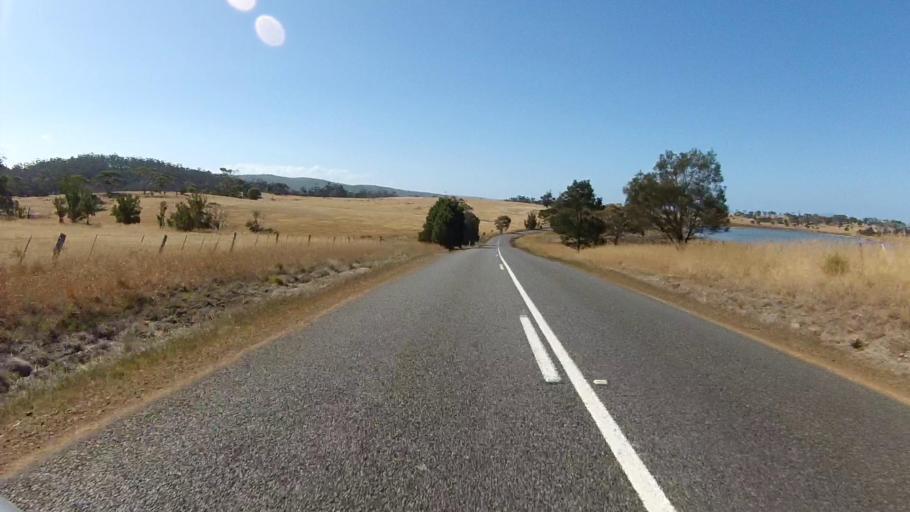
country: AU
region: Tasmania
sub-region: Sorell
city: Sorell
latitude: -42.2824
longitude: 147.9987
